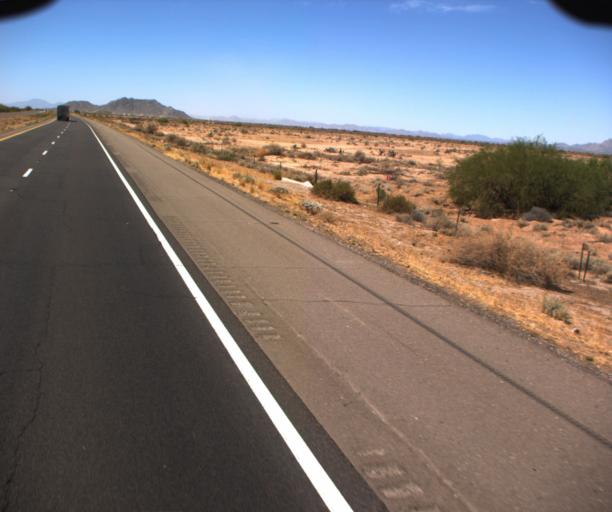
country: US
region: Arizona
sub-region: Maricopa County
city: Sun Lakes
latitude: 33.1971
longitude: -111.9962
